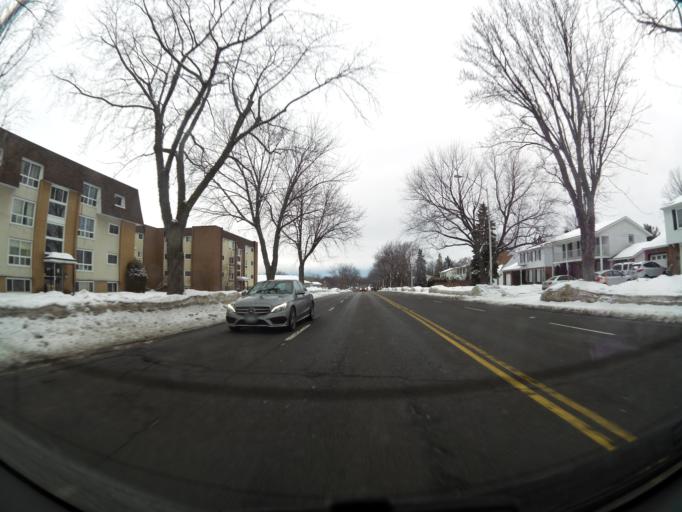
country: CA
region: Quebec
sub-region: Outaouais
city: Gatineau
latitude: 45.4534
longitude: -75.5974
